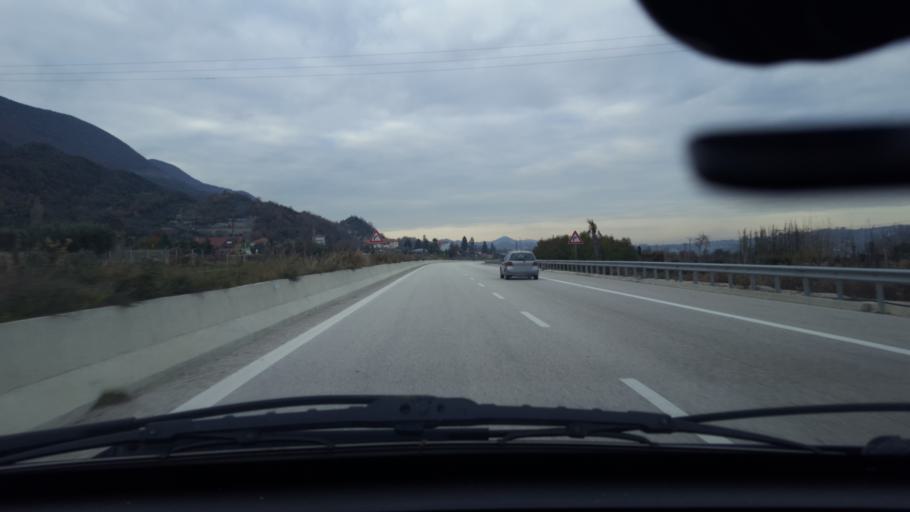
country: AL
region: Tirane
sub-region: Rrethi i Tiranes
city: Berzhite
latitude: 41.2496
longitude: 19.9008
